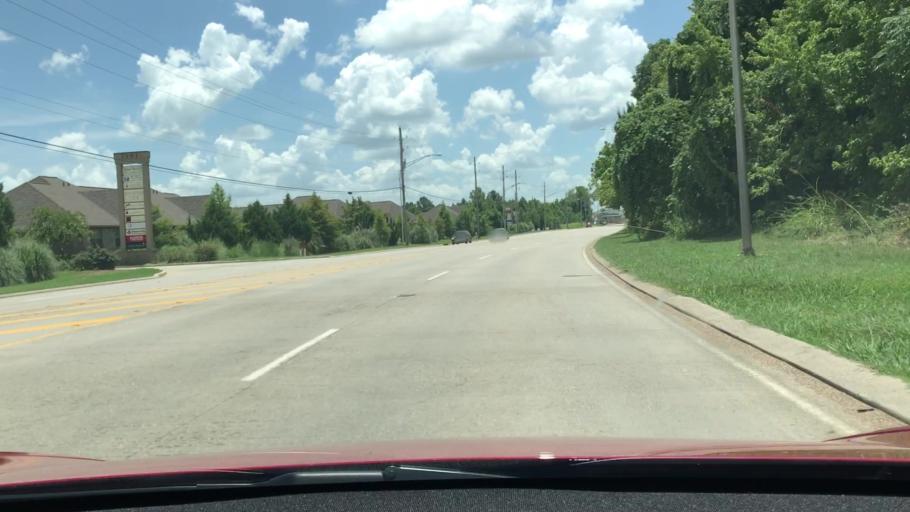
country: US
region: Louisiana
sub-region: Bossier Parish
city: Bossier City
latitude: 32.4335
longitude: -93.7264
